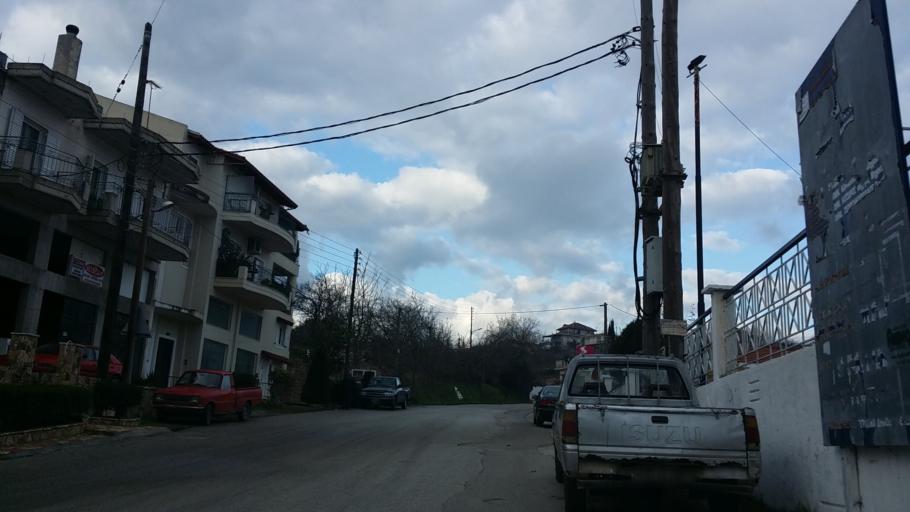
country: GR
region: West Greece
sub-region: Nomos Aitolias kai Akarnanias
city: Katouna
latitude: 38.7819
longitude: 21.1184
